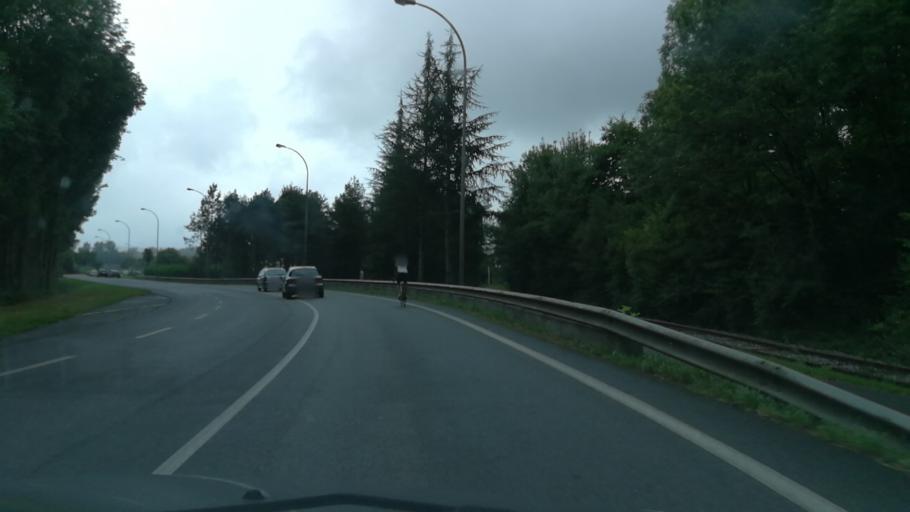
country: FR
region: Aquitaine
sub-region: Departement des Pyrenees-Atlantiques
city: Mourenx
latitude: 43.3902
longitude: -0.5801
